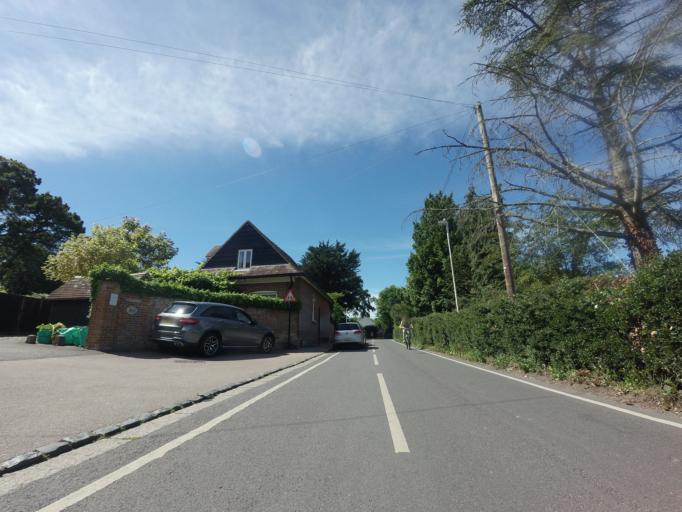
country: GB
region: England
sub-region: Kent
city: Sandwich
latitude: 51.2730
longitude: 1.3494
